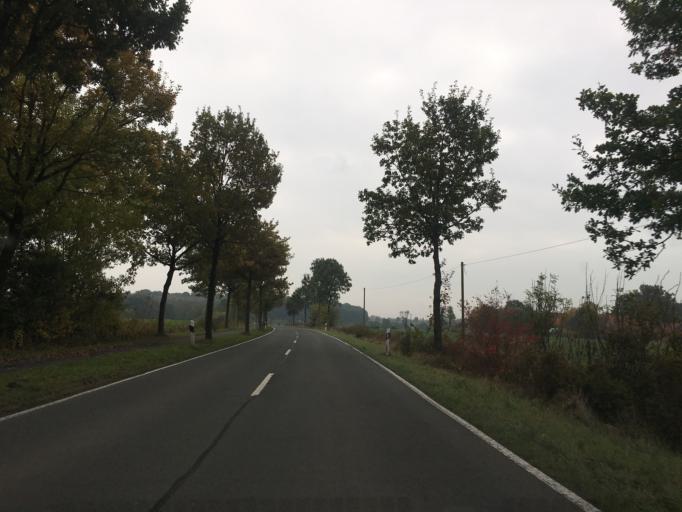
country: DE
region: North Rhine-Westphalia
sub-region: Regierungsbezirk Munster
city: Altenberge
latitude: 51.9932
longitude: 7.5297
